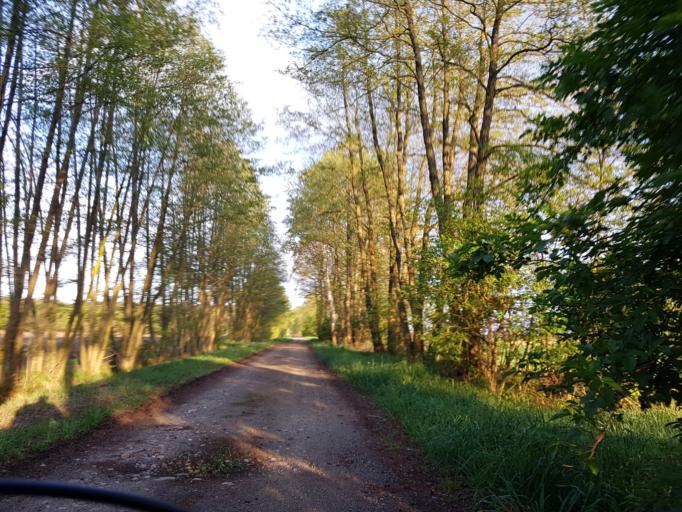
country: DE
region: Brandenburg
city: Schilda
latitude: 51.5725
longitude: 13.3761
